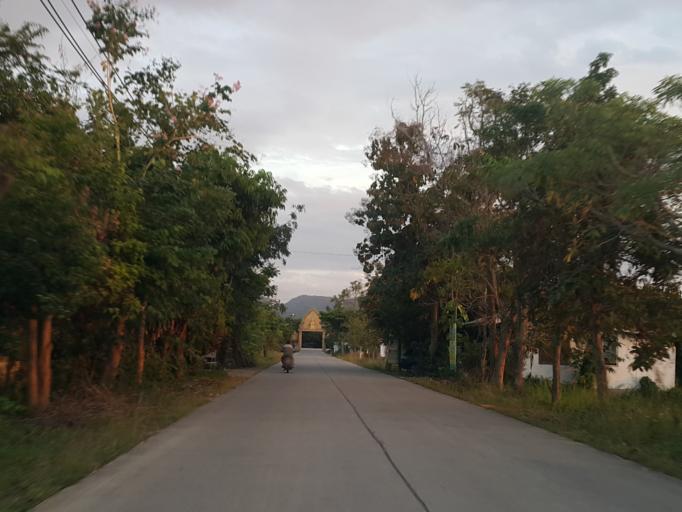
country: TH
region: Lampang
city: Mae Mo
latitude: 18.3816
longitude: 99.6026
